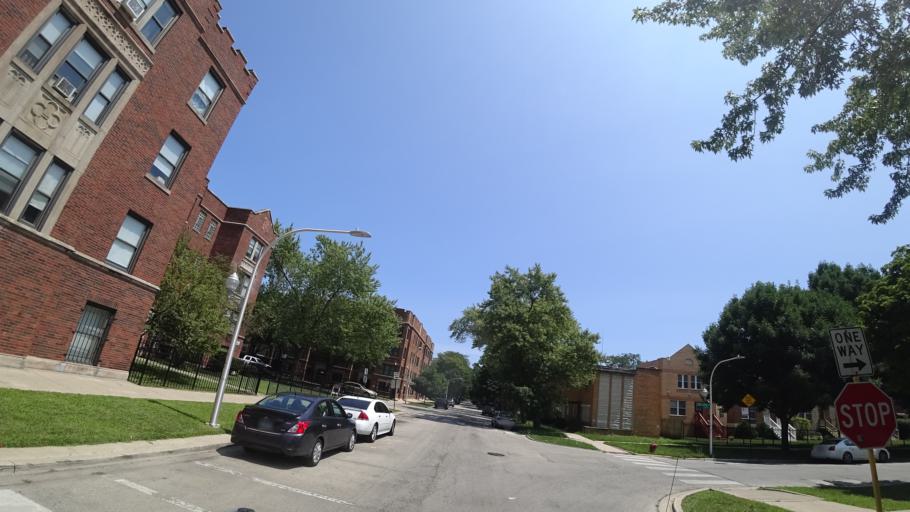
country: US
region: Illinois
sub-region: Cook County
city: Chicago
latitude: 41.7697
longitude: -87.5831
